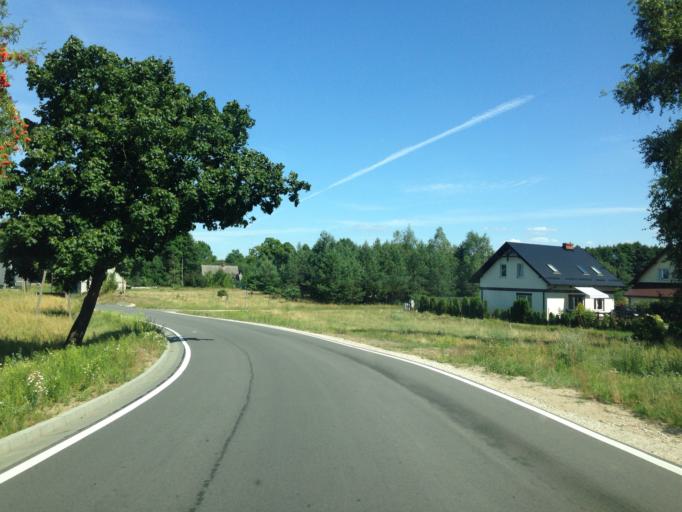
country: PL
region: Kujawsko-Pomorskie
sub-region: Powiat tucholski
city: Sliwice
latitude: 53.6378
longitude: 18.2217
